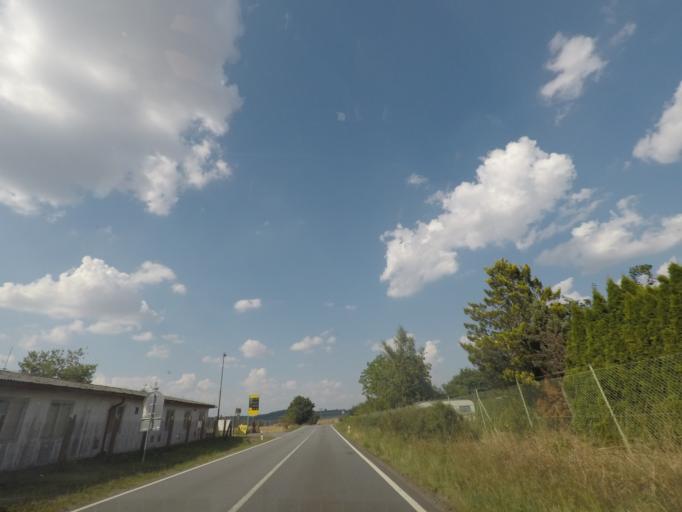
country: CZ
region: Kralovehradecky
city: Trebechovice pod Orebem
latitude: 50.2045
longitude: 15.9886
